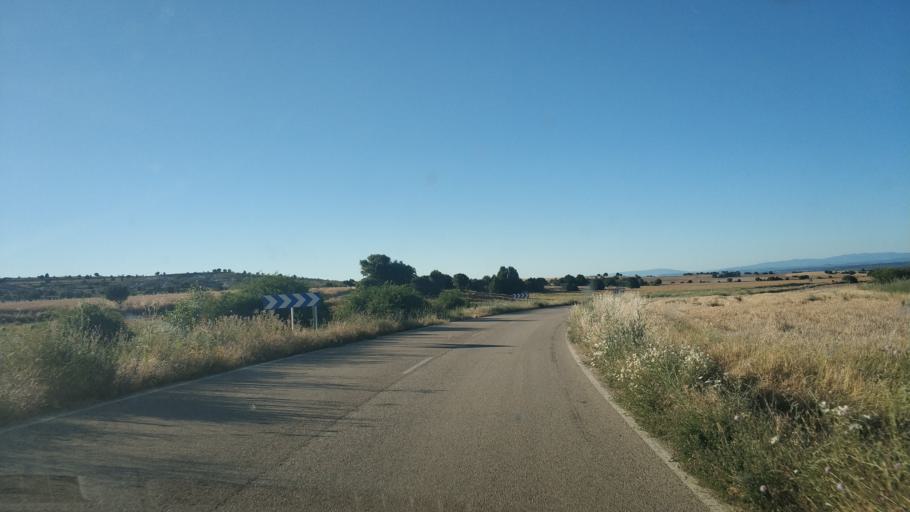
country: ES
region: Castille and Leon
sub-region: Provincia de Soria
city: San Esteban de Gormaz
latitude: 41.4778
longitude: -3.2159
